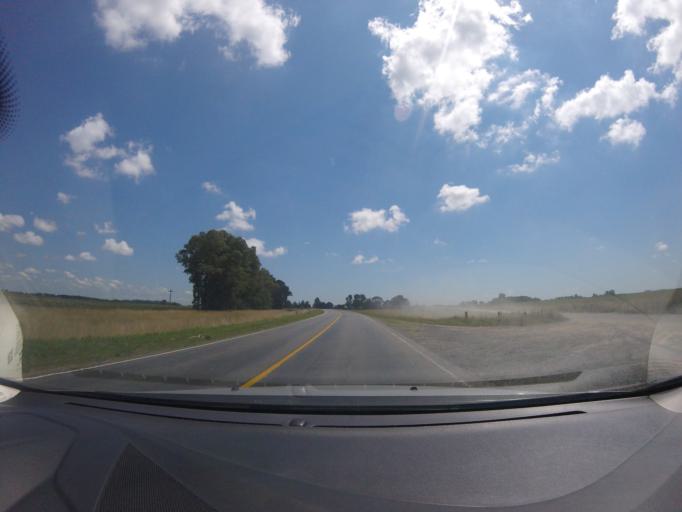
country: AR
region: Buenos Aires
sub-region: Partido de Rauch
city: Rauch
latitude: -36.7266
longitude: -59.0547
